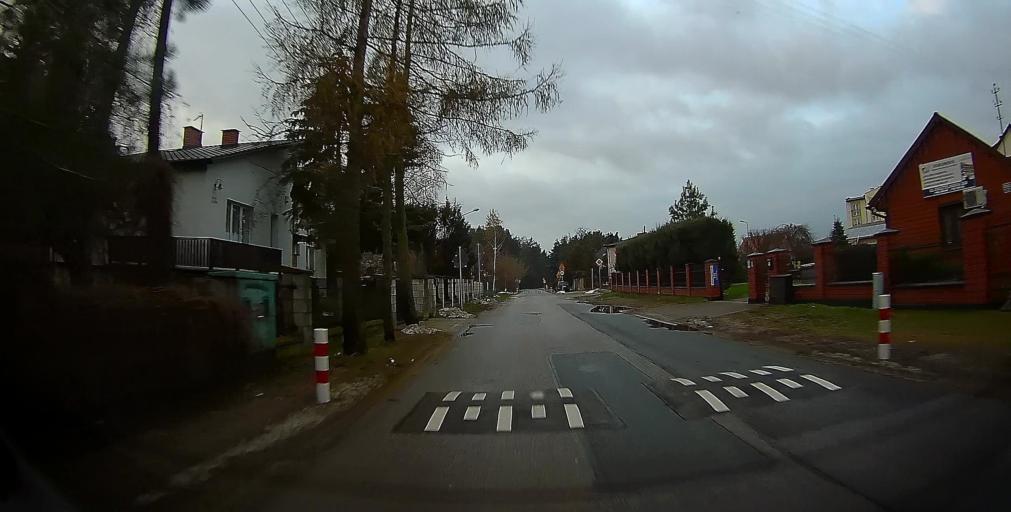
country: PL
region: Masovian Voivodeship
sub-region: Radom
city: Radom
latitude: 51.4501
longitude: 21.1349
